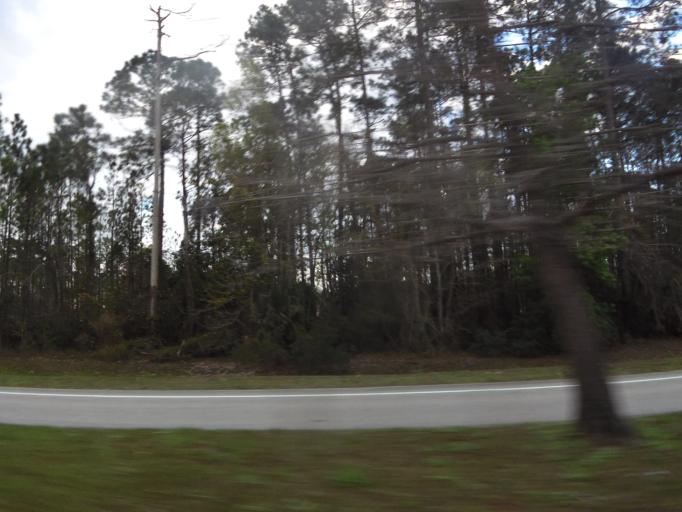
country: US
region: Florida
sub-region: Saint Johns County
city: Fruit Cove
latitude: 30.1829
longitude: -81.5717
